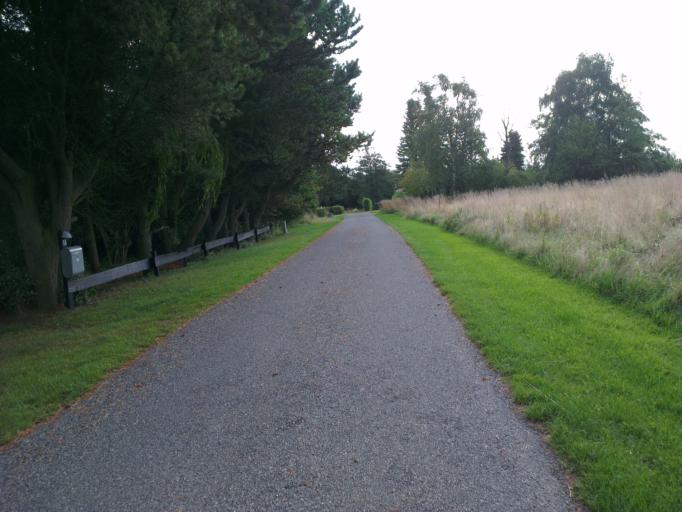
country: DK
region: Capital Region
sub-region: Frederikssund Kommune
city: Jaegerspris
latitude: 55.8295
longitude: 11.9640
